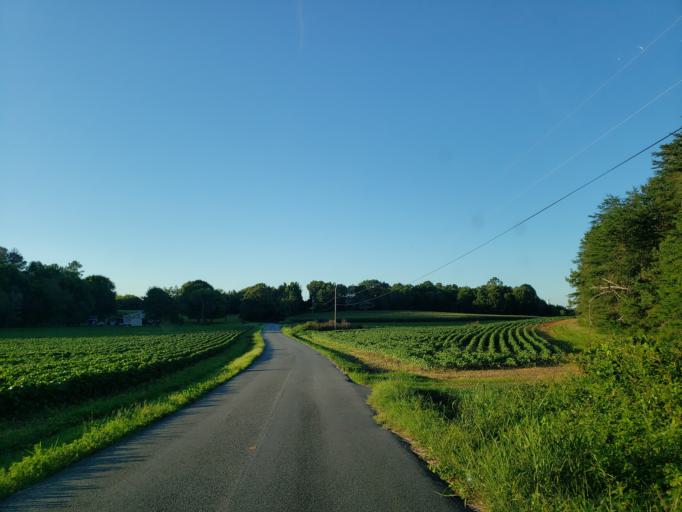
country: US
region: Georgia
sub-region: Bartow County
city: Euharlee
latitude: 34.0789
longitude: -84.9644
